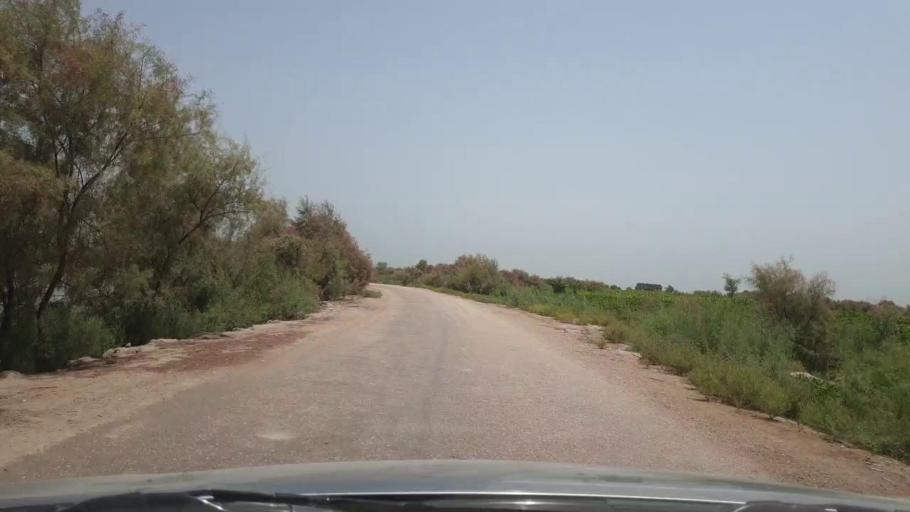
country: PK
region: Sindh
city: Pano Aqil
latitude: 27.8708
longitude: 69.1608
